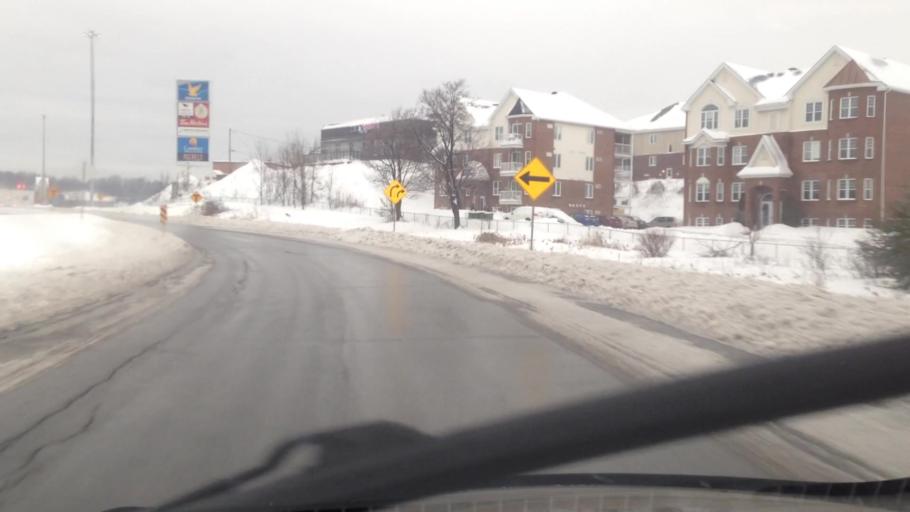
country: CA
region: Quebec
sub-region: Laurentides
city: Saint-Jerome
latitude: 45.7769
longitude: -74.0184
